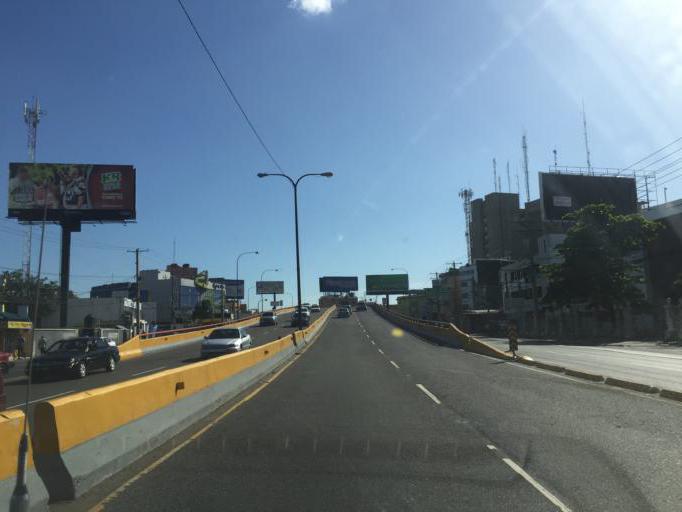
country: DO
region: Nacional
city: San Carlos
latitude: 18.4759
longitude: -69.9089
